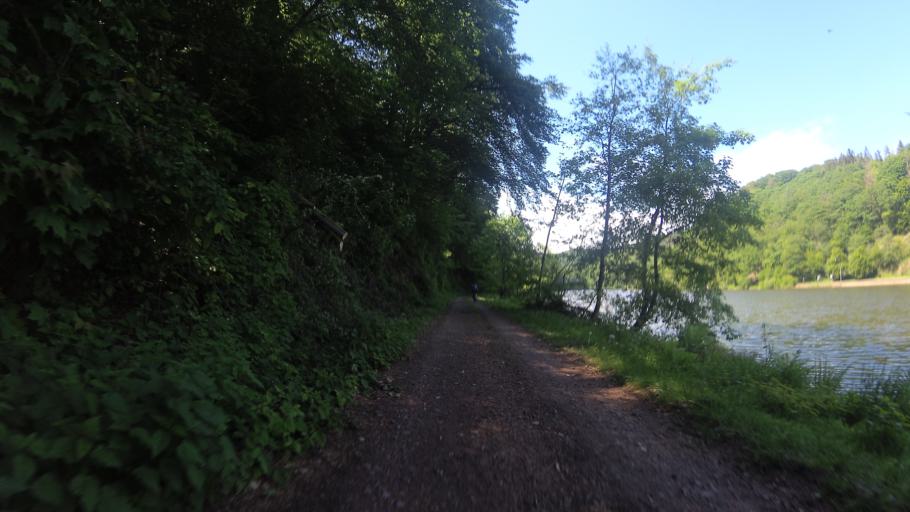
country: DE
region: Saarland
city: Mettlach
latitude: 49.4907
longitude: 6.5739
